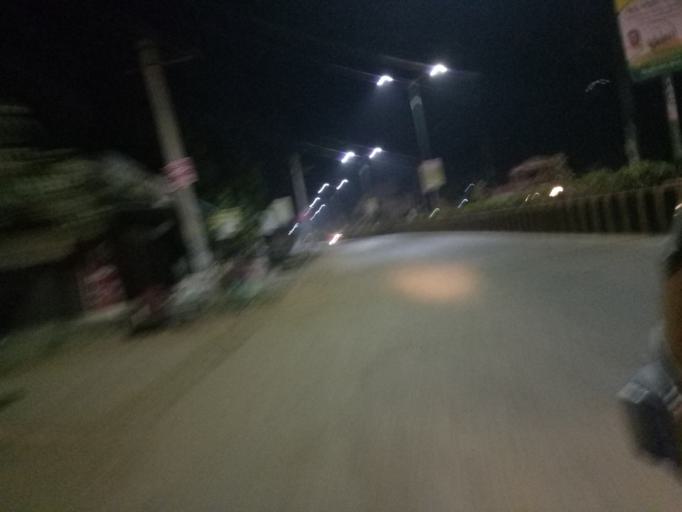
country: IN
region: Andhra Pradesh
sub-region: Nellore
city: Nellore
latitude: 14.4397
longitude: 79.9940
